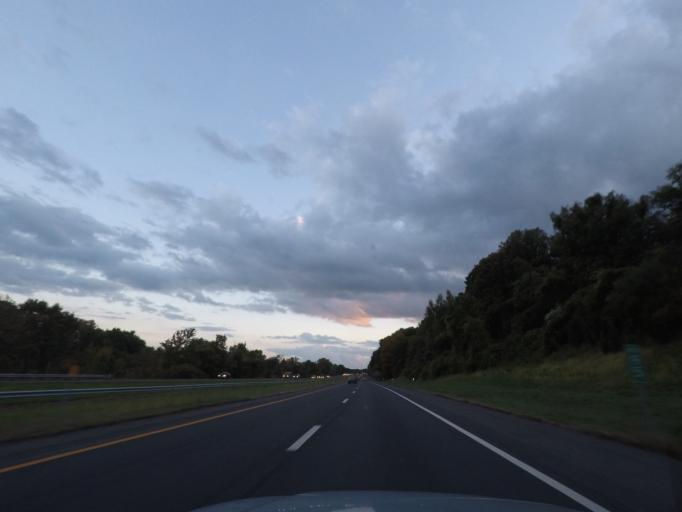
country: US
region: New York
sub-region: Ulster County
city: Lake Katrine
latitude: 41.9966
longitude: -74.0049
